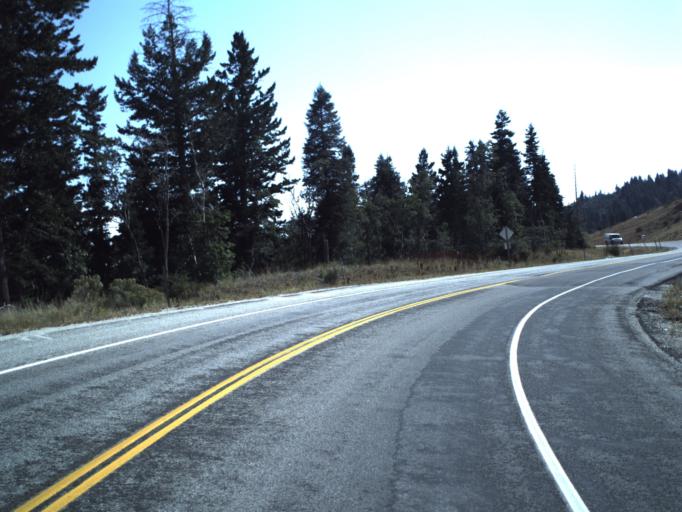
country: US
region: Utah
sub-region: Morgan County
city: Mountain Green
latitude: 41.2195
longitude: -111.8518
